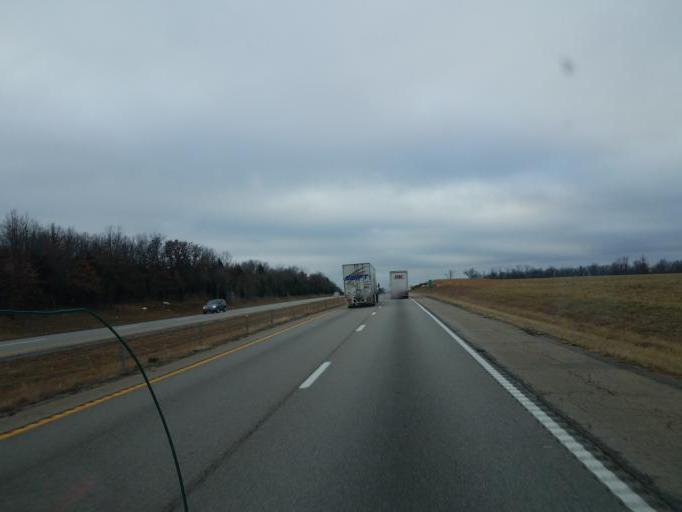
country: US
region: Missouri
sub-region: Laclede County
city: Lebanon
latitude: 37.5414
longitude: -92.8155
